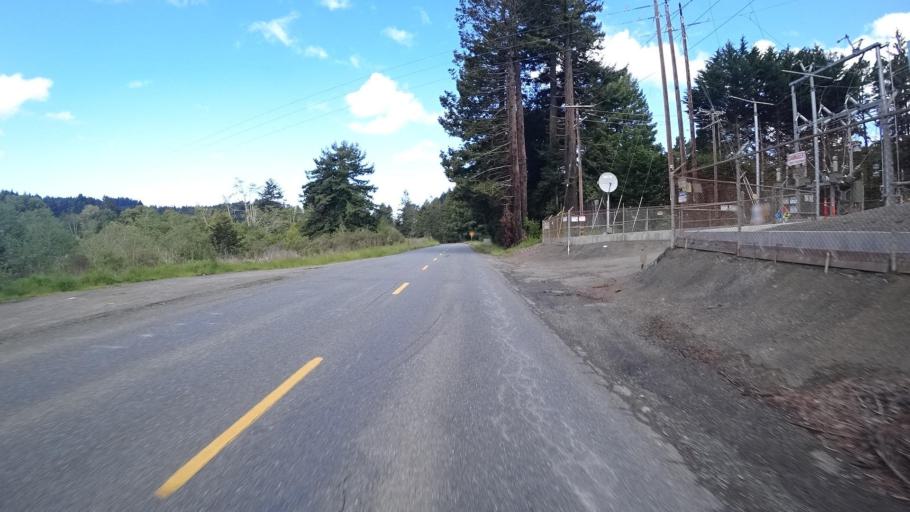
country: US
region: California
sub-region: Humboldt County
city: Blue Lake
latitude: 40.9055
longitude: -124.0344
